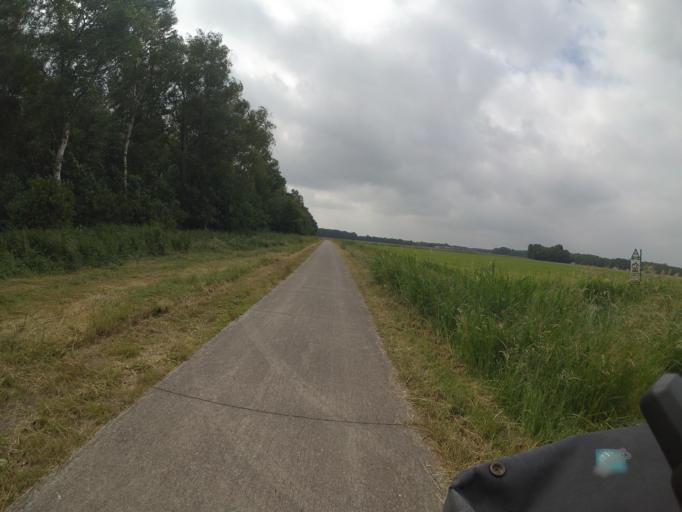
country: NL
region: Drenthe
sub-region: Gemeente Westerveld
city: Havelte
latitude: 52.8431
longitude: 6.2769
